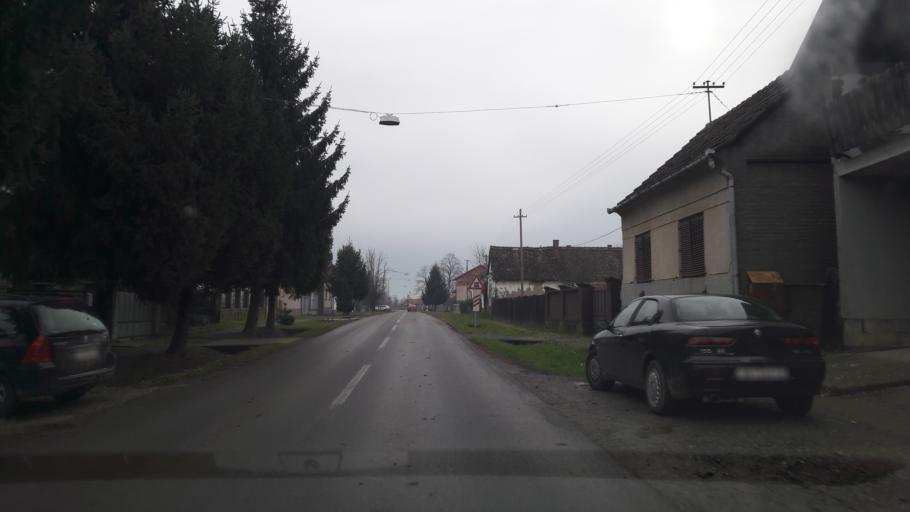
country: HR
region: Osjecko-Baranjska
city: Koska
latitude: 45.5434
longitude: 18.2918
